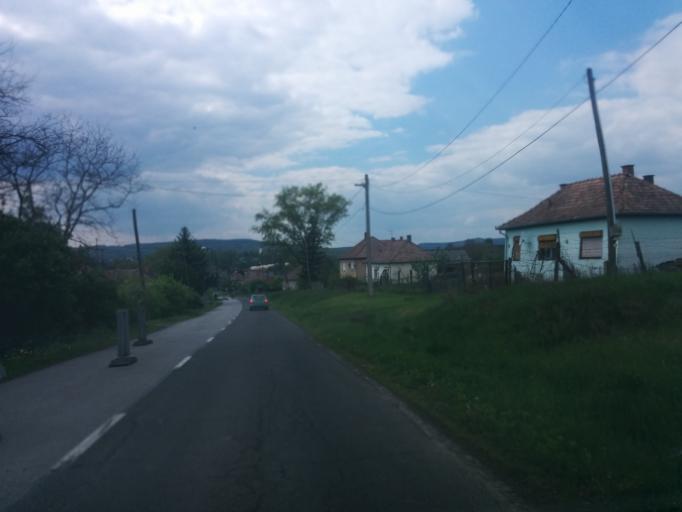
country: HU
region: Nograd
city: Bujak
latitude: 47.8277
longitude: 19.5456
